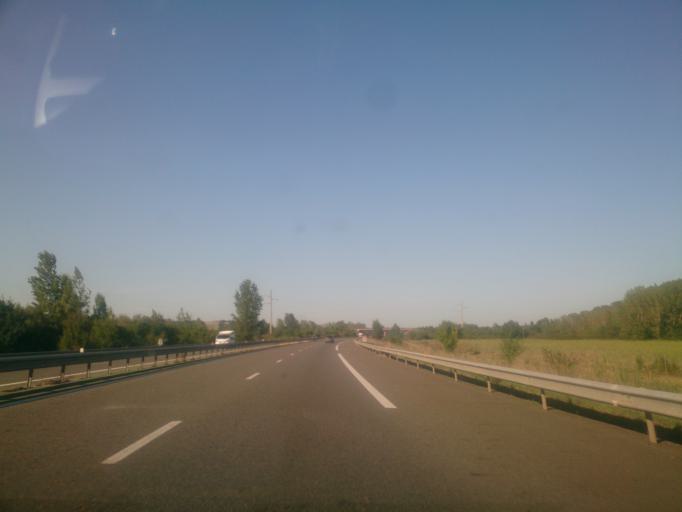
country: FR
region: Midi-Pyrenees
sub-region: Departement du Tarn-et-Garonne
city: Albias
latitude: 44.0878
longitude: 1.4231
